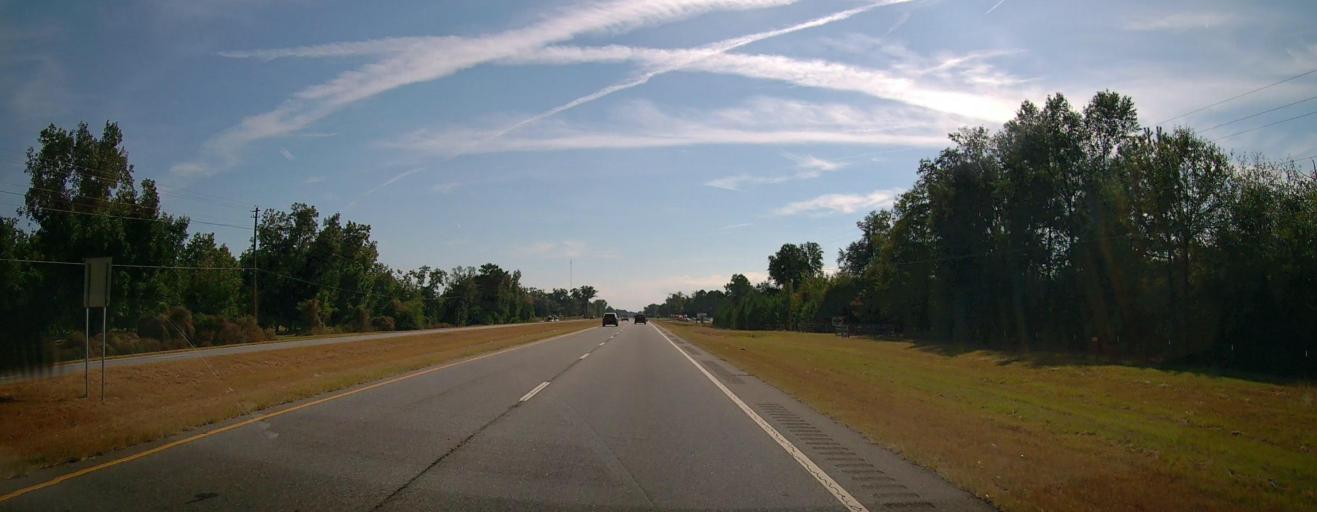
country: US
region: Georgia
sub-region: Dougherty County
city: Putney
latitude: 31.5134
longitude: -84.1156
